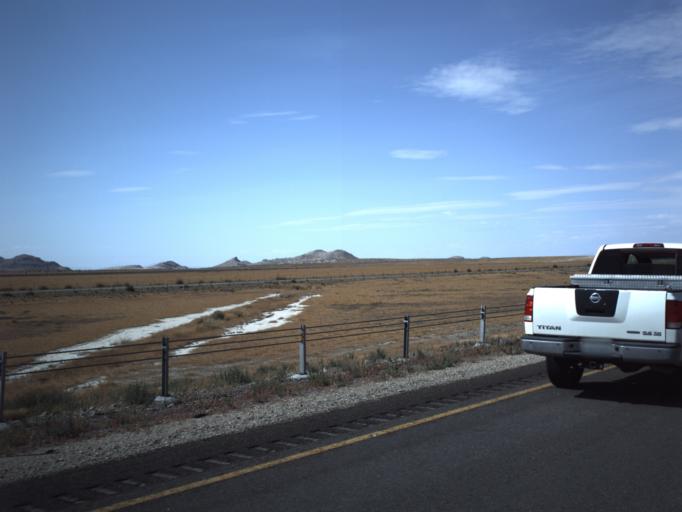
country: US
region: Utah
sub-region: Tooele County
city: Wendover
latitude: 40.7272
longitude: -113.2485
